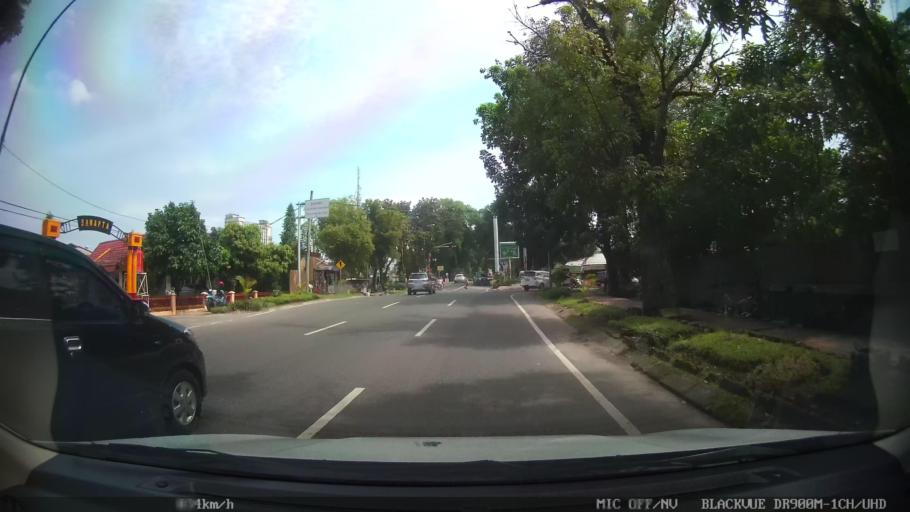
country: ID
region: North Sumatra
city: Medan
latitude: 3.5998
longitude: 98.6735
